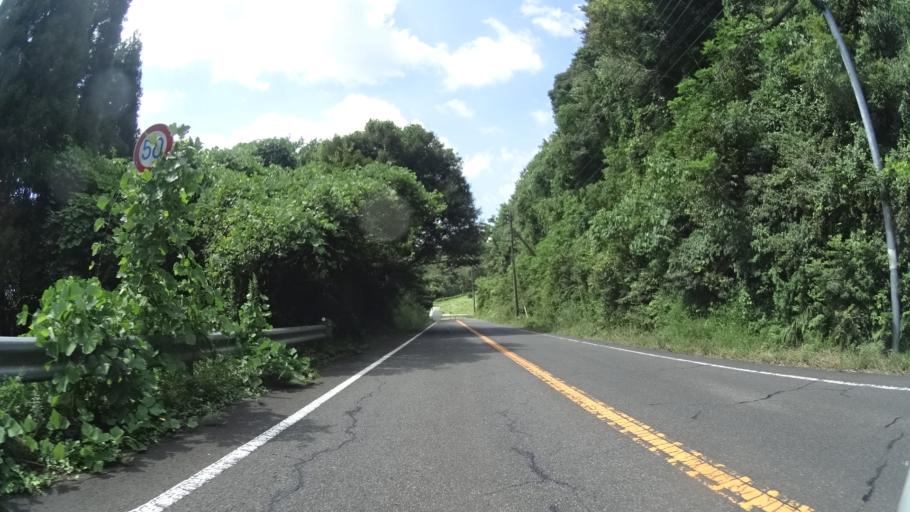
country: JP
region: Kagoshima
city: Kokubu-matsuki
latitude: 31.8748
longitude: 130.7971
